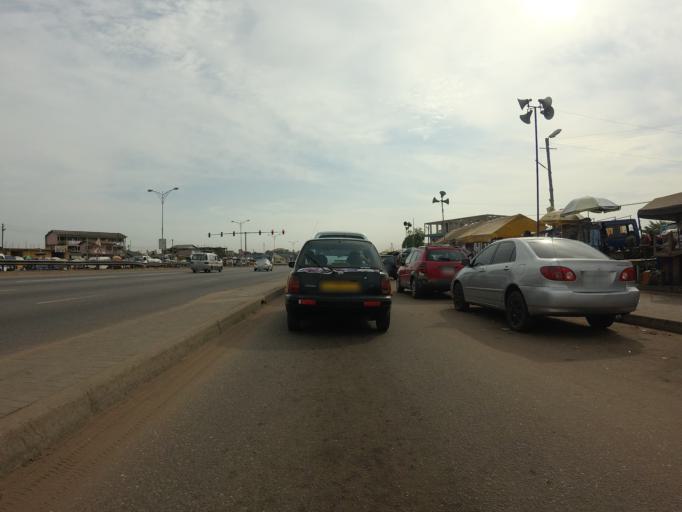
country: GH
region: Greater Accra
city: Dome
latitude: 5.6074
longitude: -0.2469
